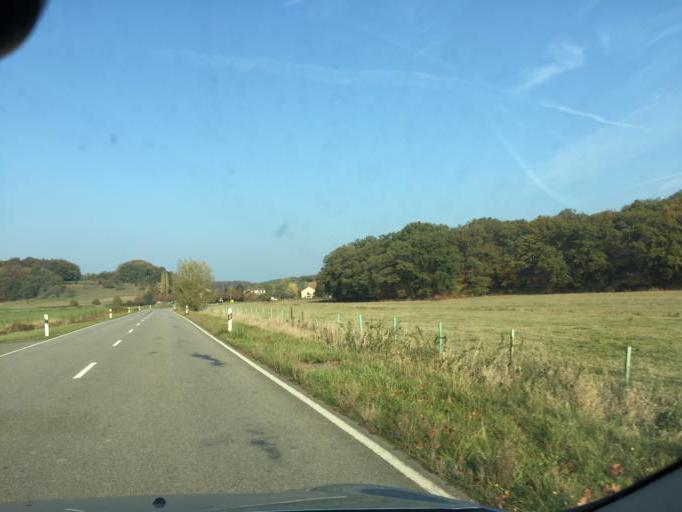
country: LU
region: Luxembourg
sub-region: Canton de Luxembourg
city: Contern
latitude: 49.5573
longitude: 6.2259
